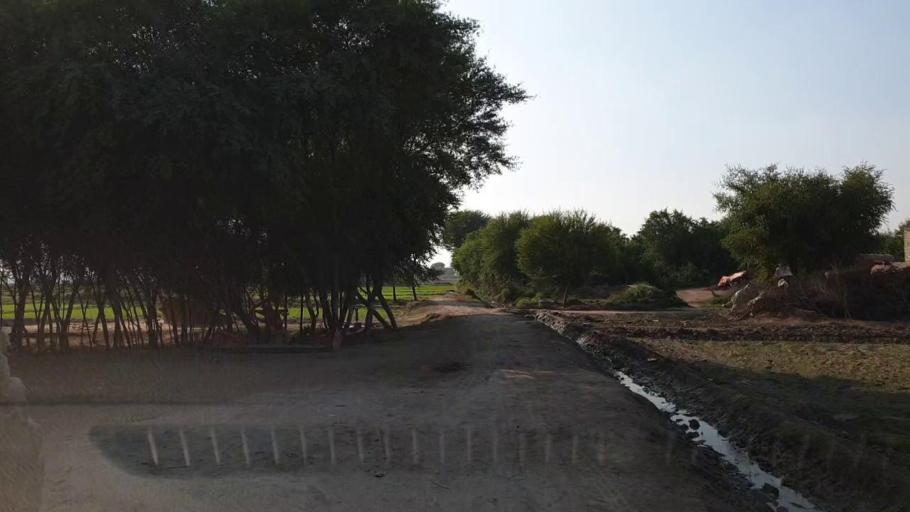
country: PK
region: Sindh
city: Sehwan
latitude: 26.4373
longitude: 67.8112
